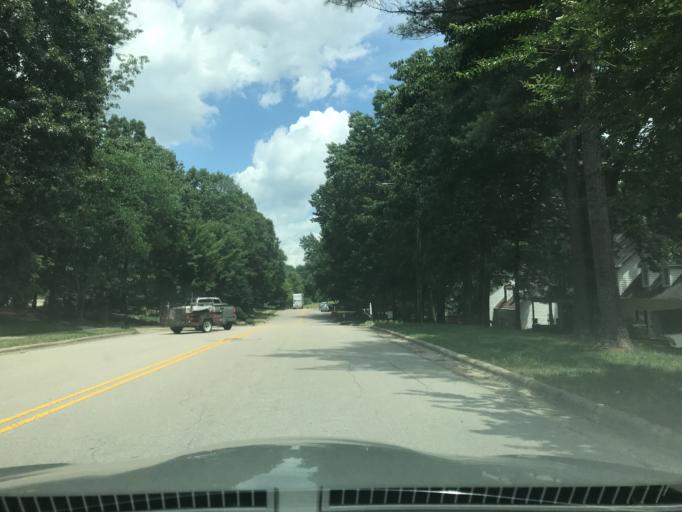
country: US
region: North Carolina
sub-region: Wake County
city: West Raleigh
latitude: 35.8901
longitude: -78.6052
